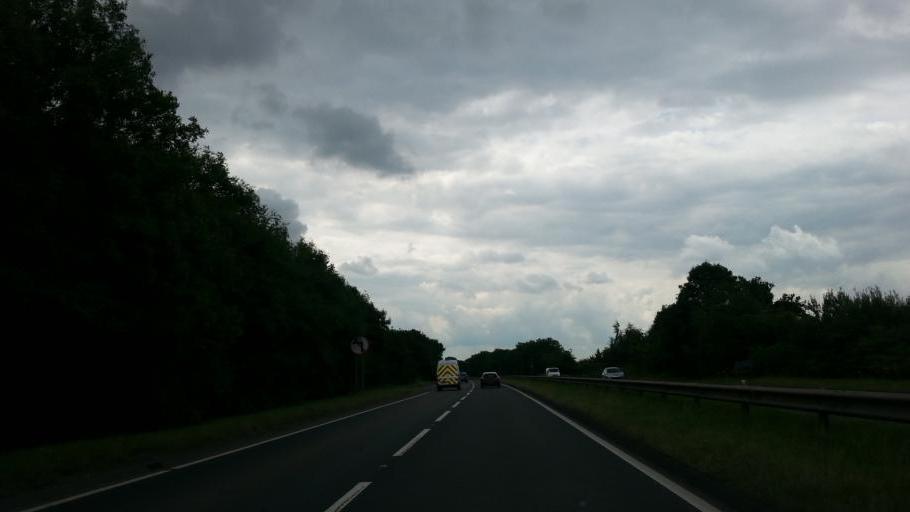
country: GB
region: England
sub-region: City and Borough of Birmingham
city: Sutton Coldfield
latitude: 52.6025
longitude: -1.7957
